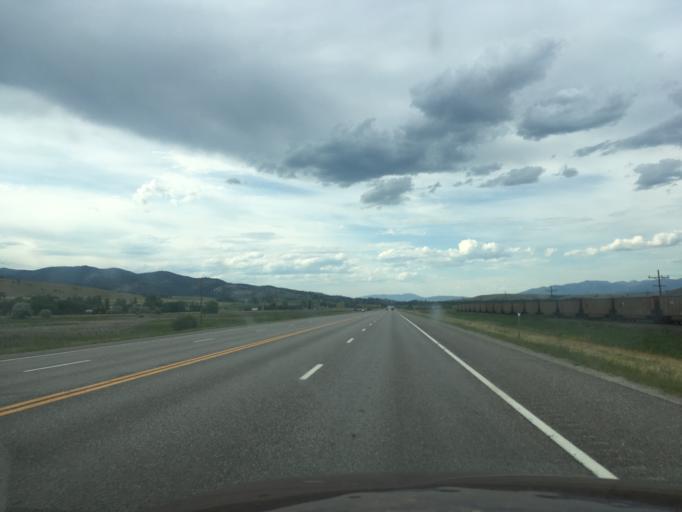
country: US
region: Montana
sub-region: Missoula County
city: Lolo
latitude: 46.7184
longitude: -114.0772
